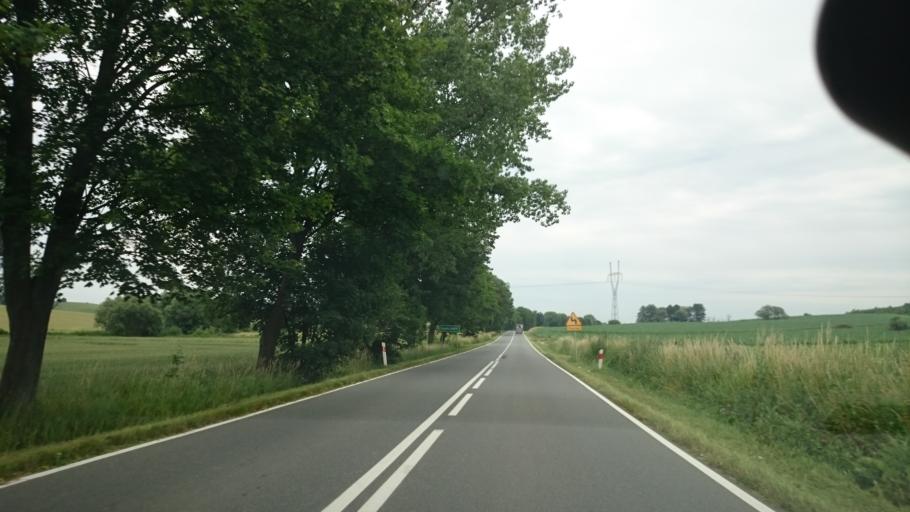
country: PL
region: Lower Silesian Voivodeship
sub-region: Powiat zabkowicki
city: Ziebice
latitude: 50.5873
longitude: 16.9663
